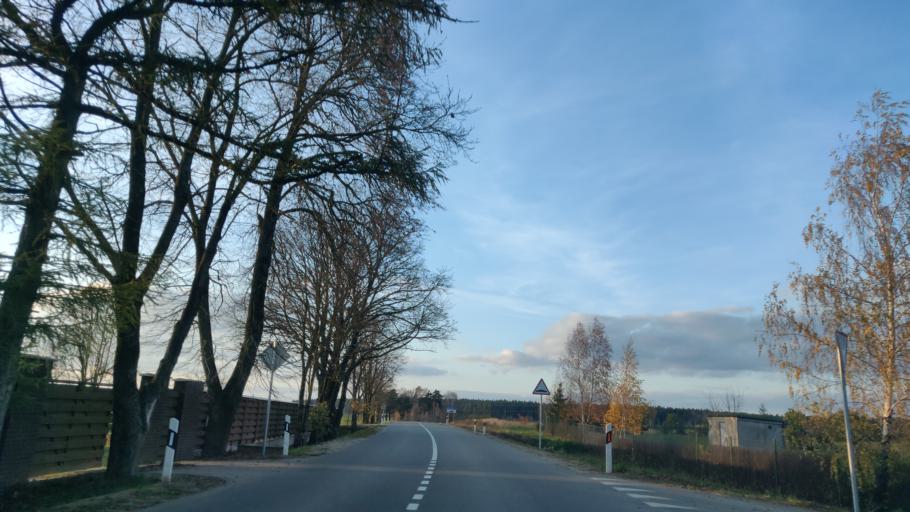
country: LT
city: Lentvaris
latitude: 54.5917
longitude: 25.0478
